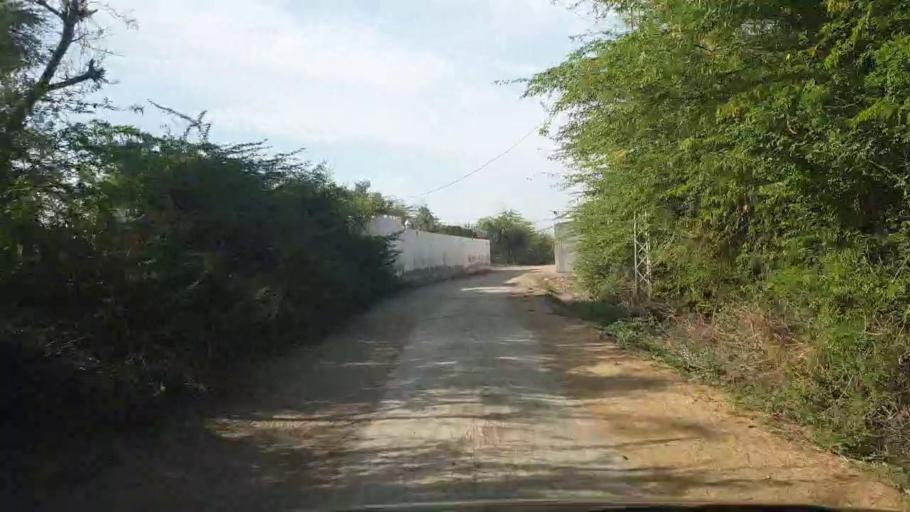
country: PK
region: Sindh
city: Umarkot
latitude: 25.3314
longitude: 69.7033
